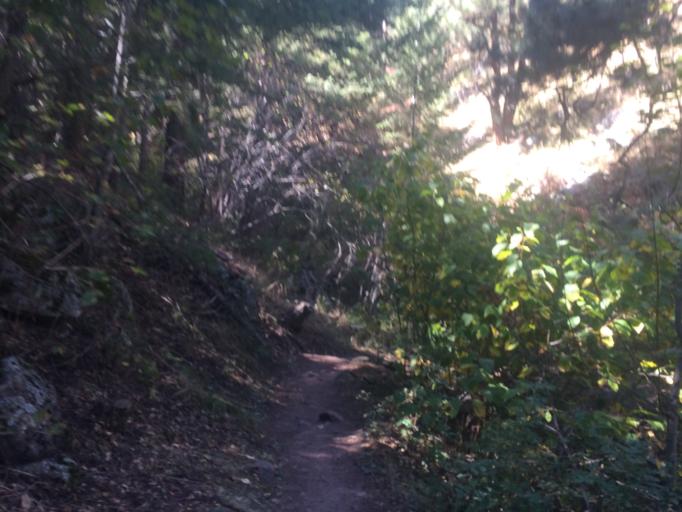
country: US
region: Colorado
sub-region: Boulder County
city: Boulder
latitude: 39.9652
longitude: -105.2804
